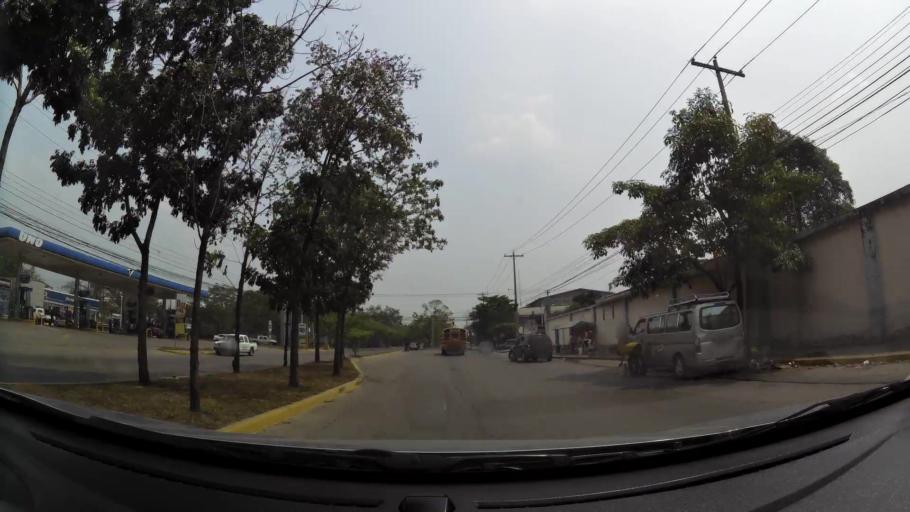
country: HN
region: Cortes
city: San Pedro Sula
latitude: 15.4871
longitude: -88.0242
